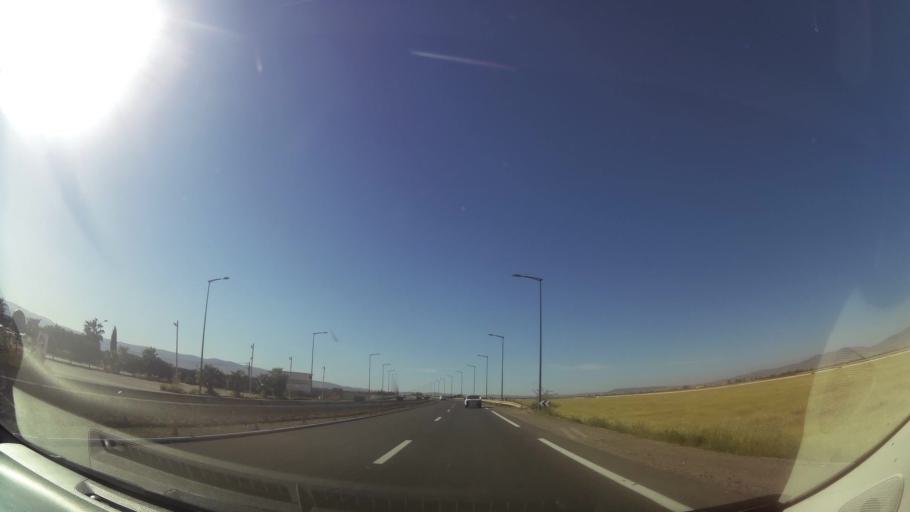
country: MA
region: Oriental
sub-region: Oujda-Angad
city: Oujda
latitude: 34.8060
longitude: -1.9582
